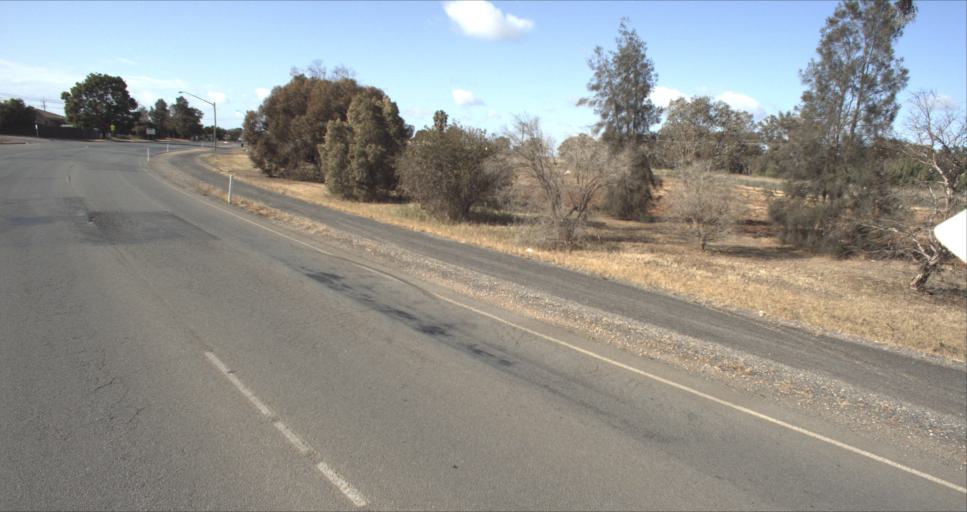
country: AU
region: New South Wales
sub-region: Leeton
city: Leeton
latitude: -34.5600
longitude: 146.3920
